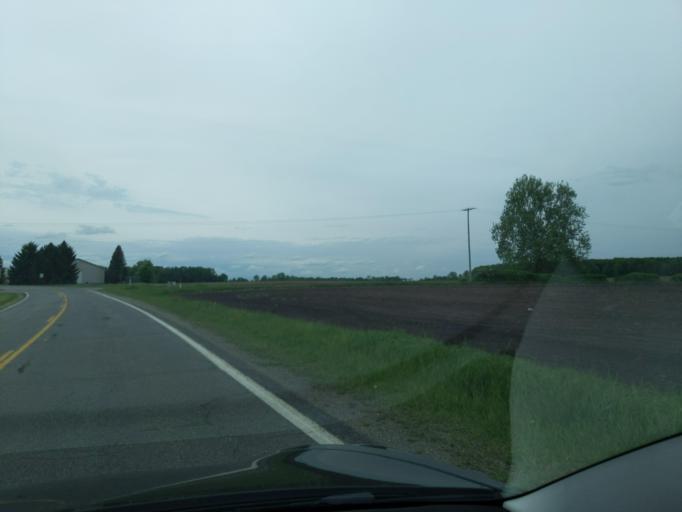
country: US
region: Michigan
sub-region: Ingham County
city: Mason
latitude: 42.5522
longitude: -84.4233
